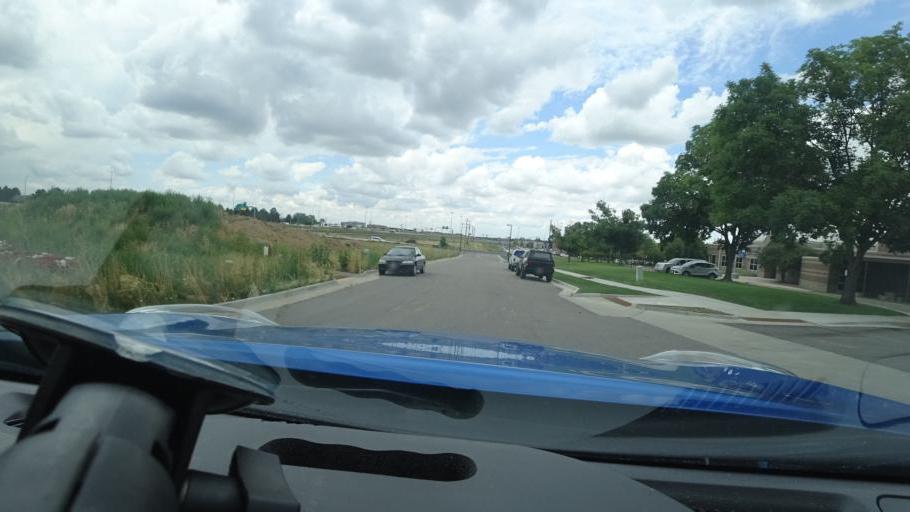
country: US
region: Colorado
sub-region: Adams County
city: Aurora
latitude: 39.7208
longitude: -104.8241
